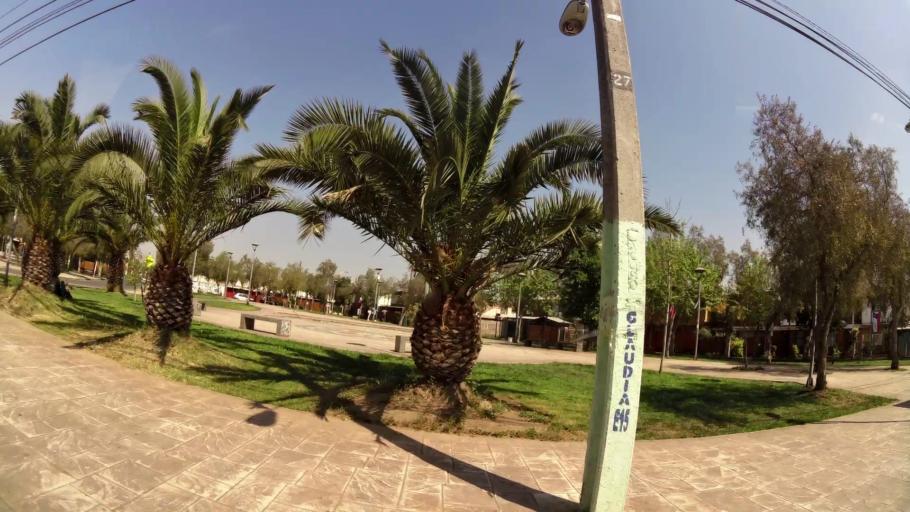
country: CL
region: Santiago Metropolitan
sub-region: Provincia de Santiago
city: La Pintana
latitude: -33.5520
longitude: -70.6153
